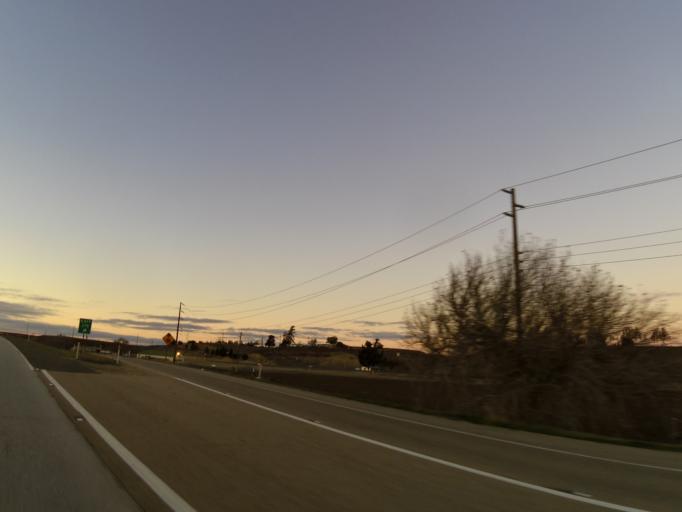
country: US
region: California
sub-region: Monterey County
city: King City
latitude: 36.1855
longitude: -121.0697
